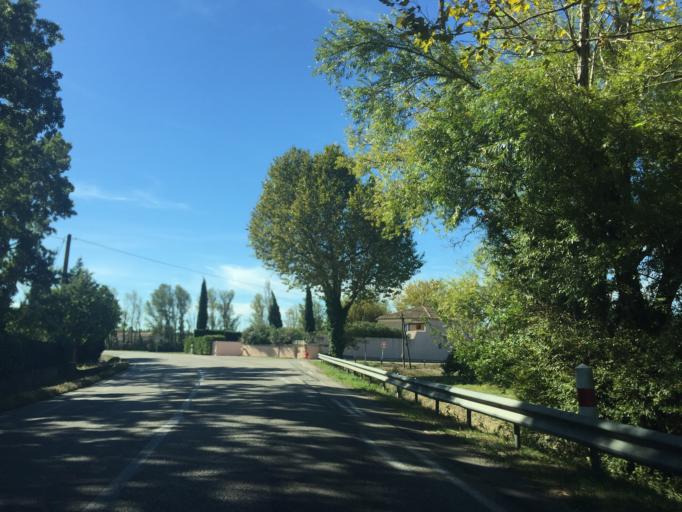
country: FR
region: Provence-Alpes-Cote d'Azur
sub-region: Departement du Vaucluse
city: Caderousse
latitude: 44.1091
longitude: 4.7630
